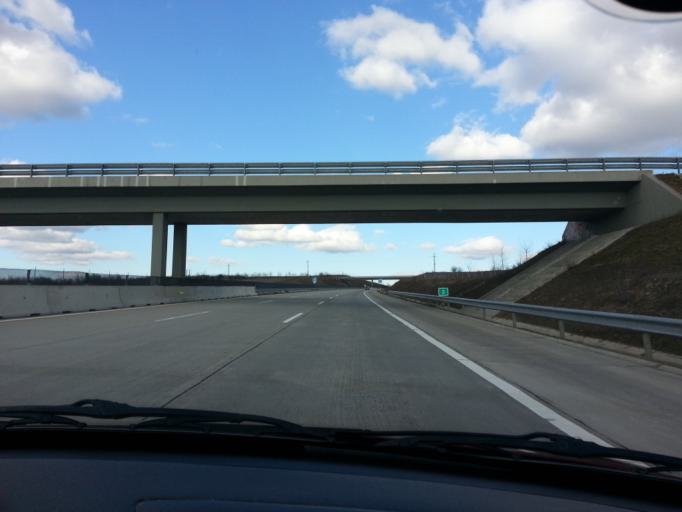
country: HU
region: Pest
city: Nagytarcsa
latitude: 47.5307
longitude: 19.3046
